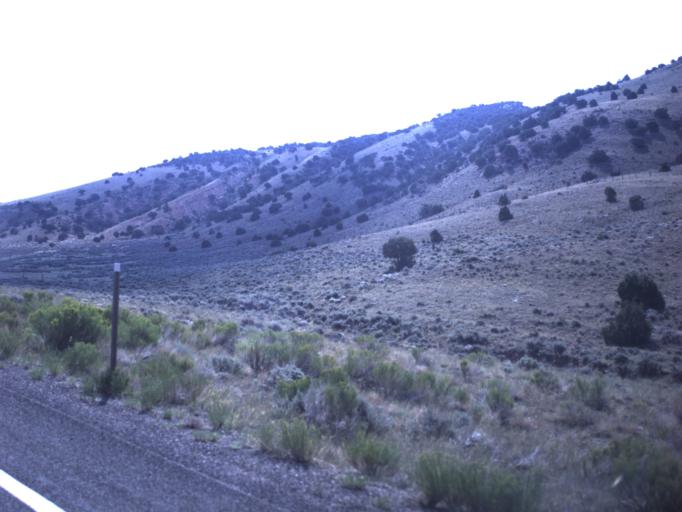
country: US
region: Utah
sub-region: Daggett County
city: Manila
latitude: 40.9311
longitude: -109.7066
